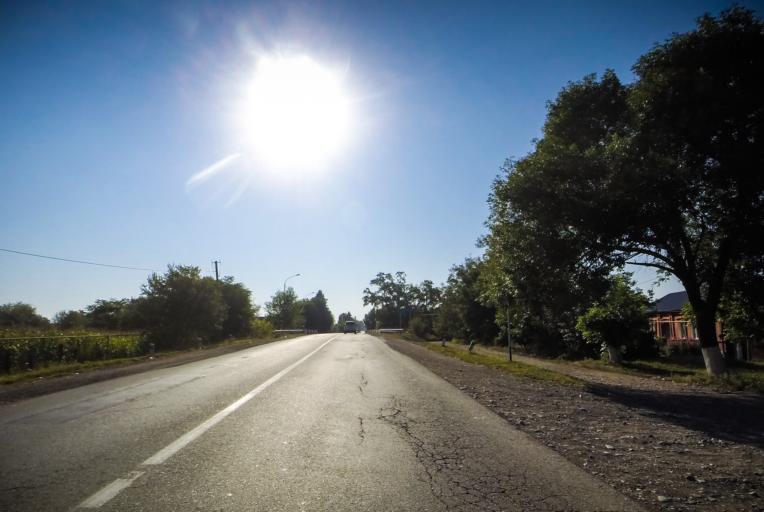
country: RU
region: North Ossetia
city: Ardon
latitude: 43.1416
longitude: 44.3971
